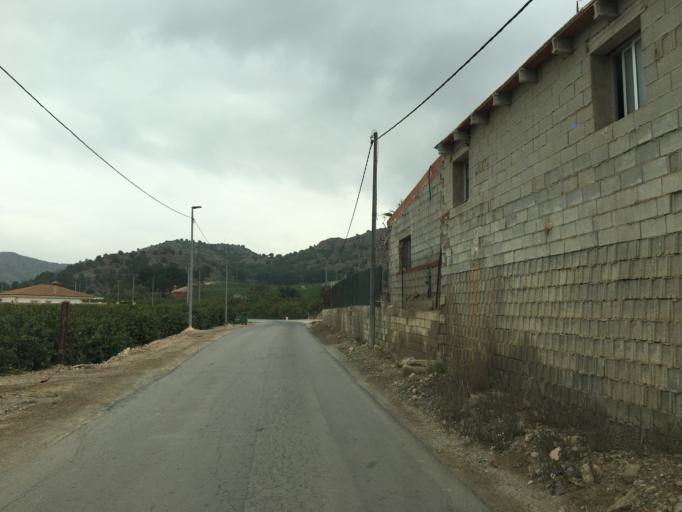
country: ES
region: Murcia
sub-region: Murcia
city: Santomera
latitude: 38.0779
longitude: -1.0467
